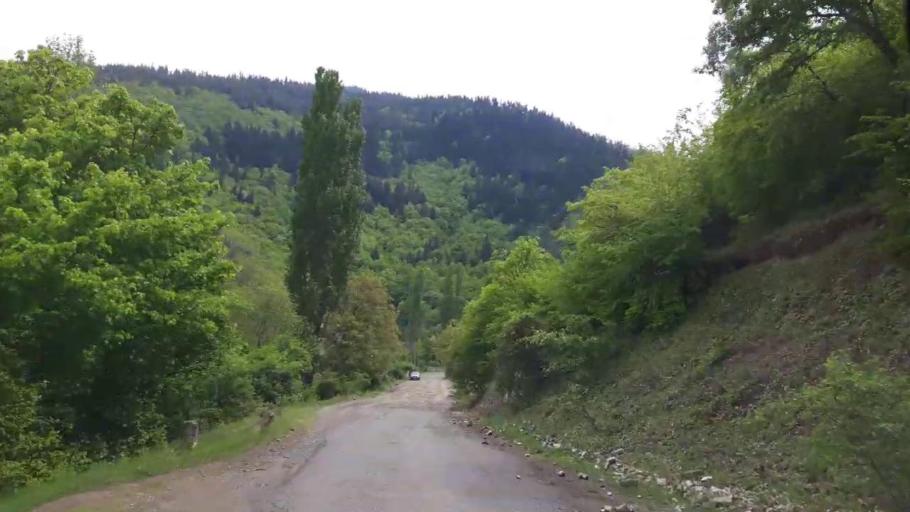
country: GE
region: Shida Kartli
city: Gori
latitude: 41.8852
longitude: 43.9975
